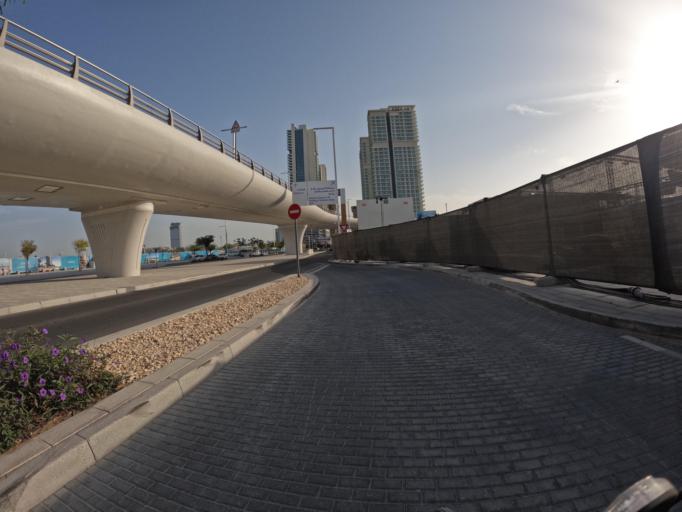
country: AE
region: Dubai
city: Dubai
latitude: 25.0953
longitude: 55.1377
